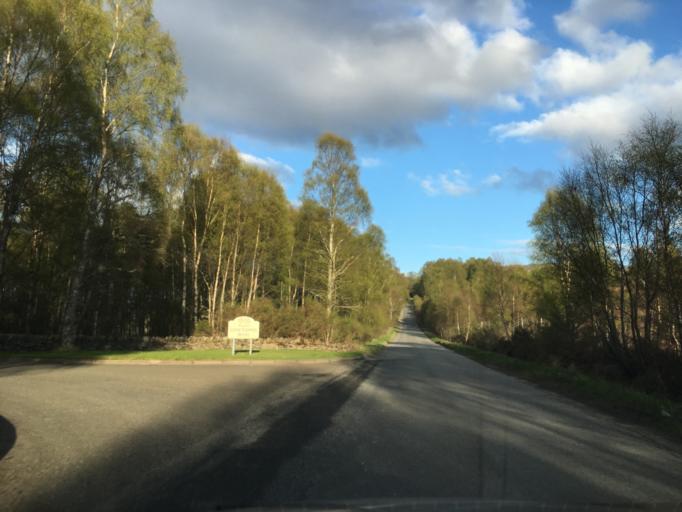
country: GB
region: Scotland
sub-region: Perth and Kinross
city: Aberfeldy
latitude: 56.7052
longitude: -4.0068
